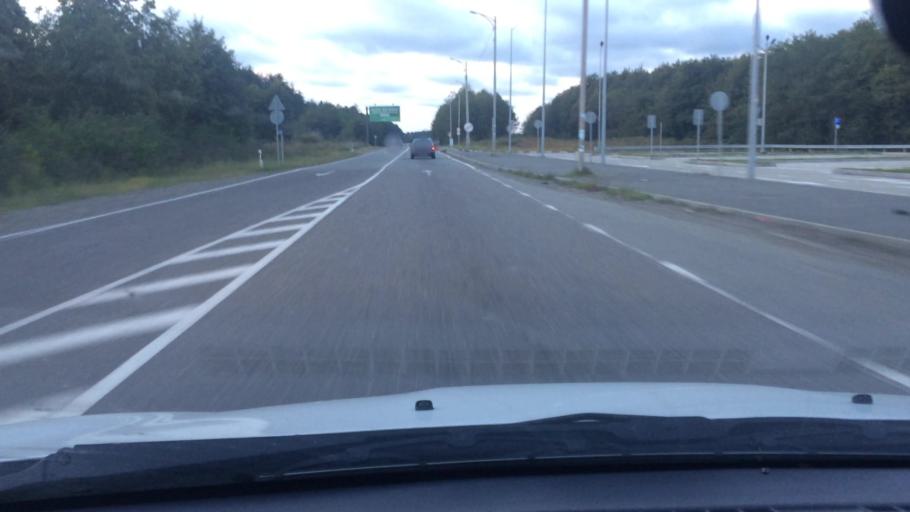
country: GE
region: Guria
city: Urek'i
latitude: 41.9399
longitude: 41.7712
